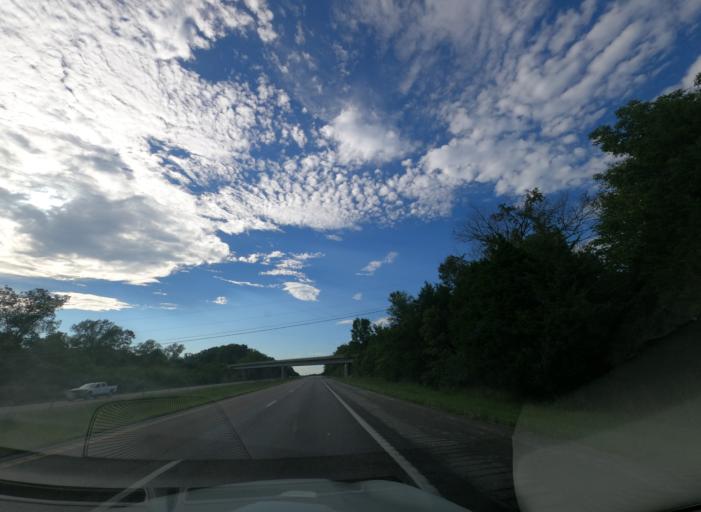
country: US
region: Missouri
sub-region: Jefferson County
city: Crystal City
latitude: 38.1382
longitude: -90.3272
